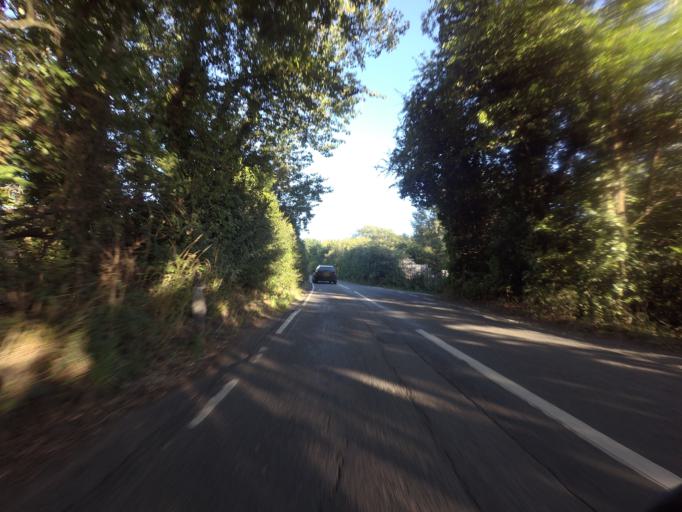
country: GB
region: England
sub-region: Kent
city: Sturry
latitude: 51.3276
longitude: 1.1930
